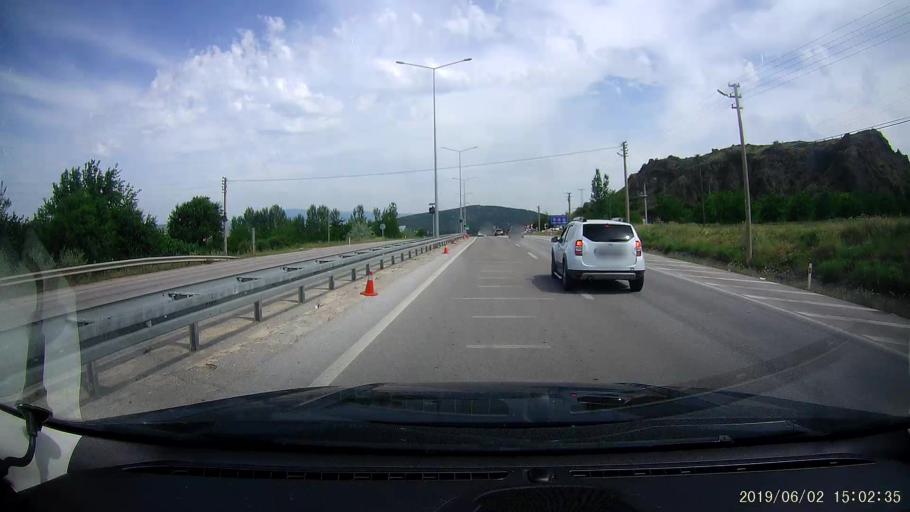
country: TR
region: Corum
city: Osmancik
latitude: 40.9797
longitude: 34.7691
